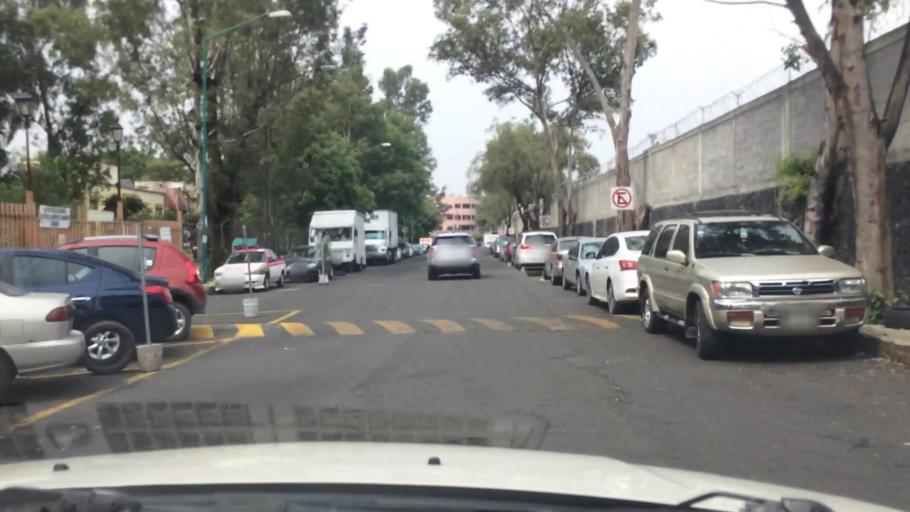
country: MX
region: Mexico City
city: Xochimilco
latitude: 19.2718
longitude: -99.1235
